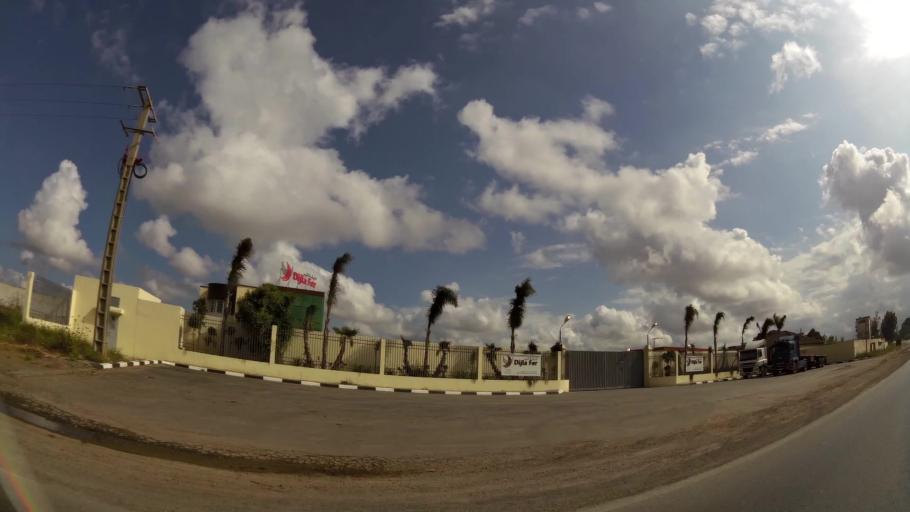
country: MA
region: Gharb-Chrarda-Beni Hssen
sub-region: Kenitra Province
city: Kenitra
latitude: 34.2816
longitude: -6.5372
